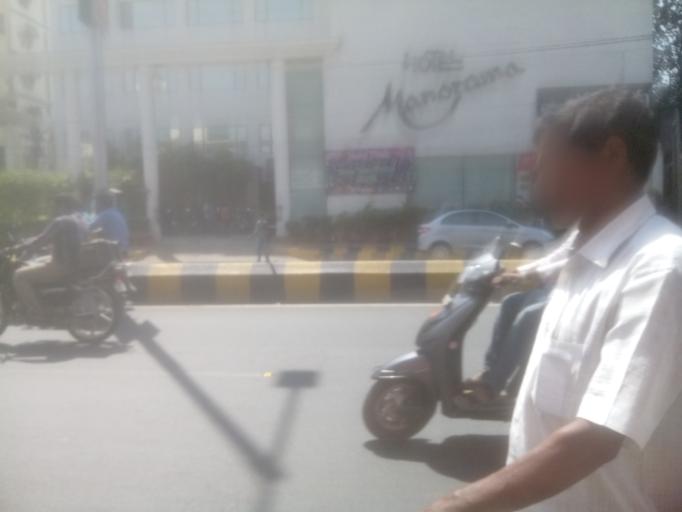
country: IN
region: Andhra Pradesh
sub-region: Krishna
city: Vijayawada
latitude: 16.5113
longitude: 80.6201
